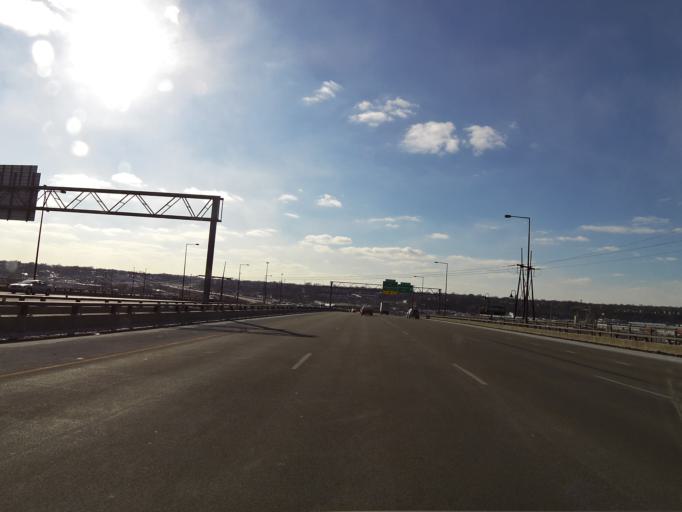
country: US
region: Minnesota
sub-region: Dakota County
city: South Saint Paul
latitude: 44.8830
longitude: -93.0167
